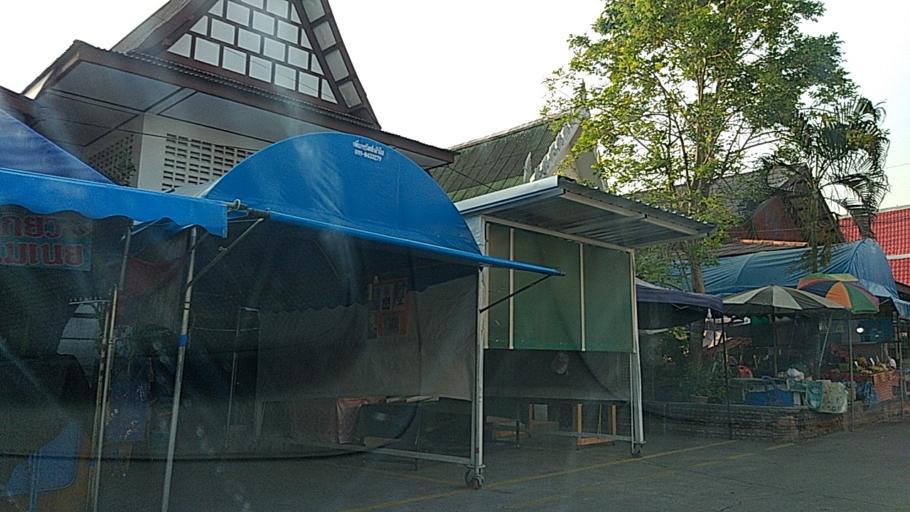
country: TH
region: Phra Nakhon Si Ayutthaya
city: Ban Bang Kadi Pathum Thani
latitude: 14.0032
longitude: 100.5415
